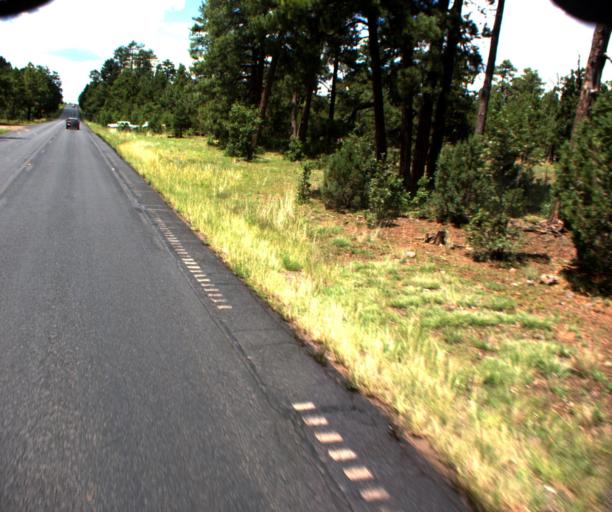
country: US
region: Arizona
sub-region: Gila County
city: Pine
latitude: 34.5022
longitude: -111.4653
